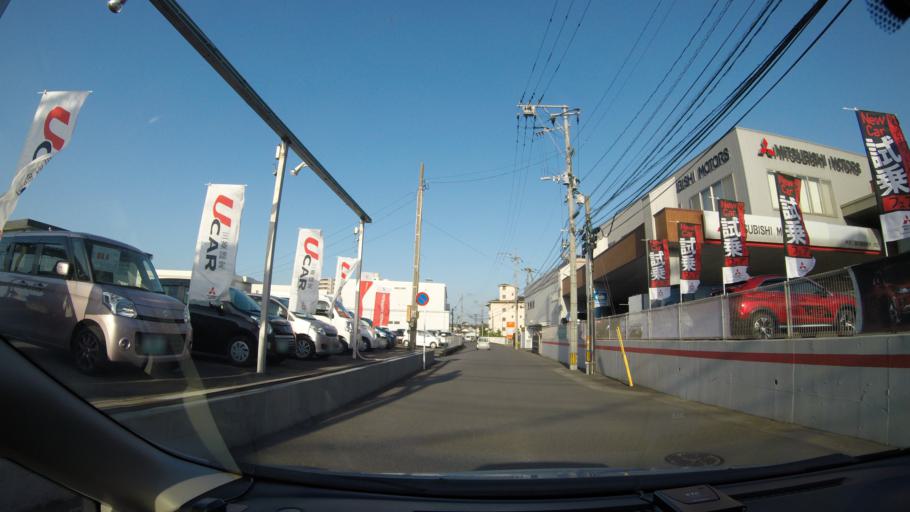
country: JP
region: Oita
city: Oita
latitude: 33.2113
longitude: 131.6079
